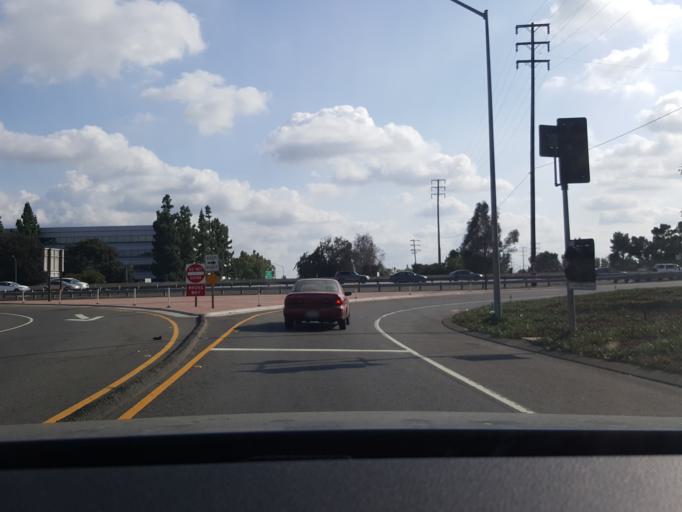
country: US
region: California
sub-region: Los Angeles County
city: Rosemead
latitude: 34.0732
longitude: -118.0724
